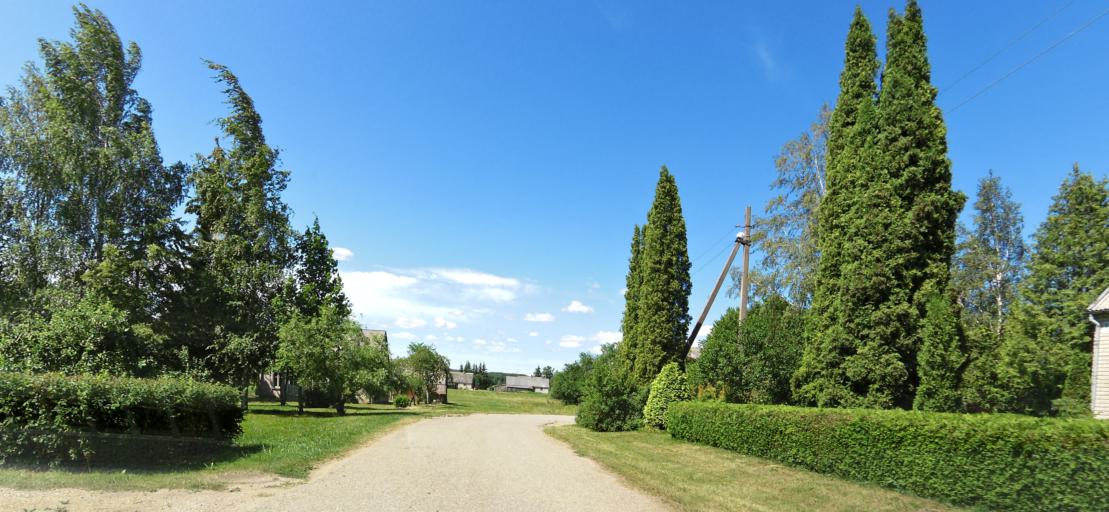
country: LT
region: Panevezys
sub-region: Birzai
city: Birzai
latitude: 56.2521
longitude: 24.5398
